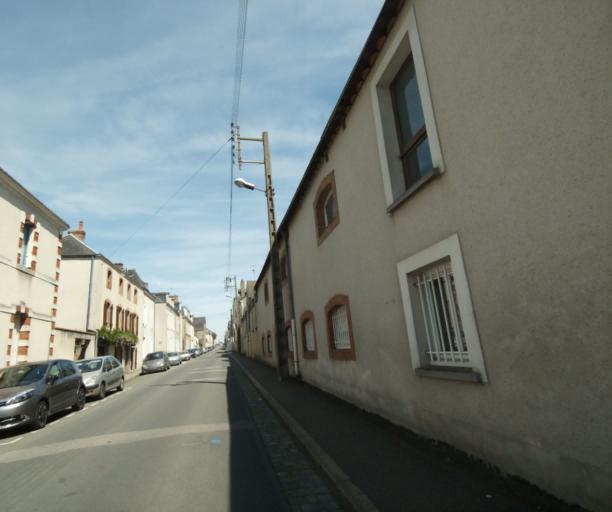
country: FR
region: Pays de la Loire
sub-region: Departement de la Mayenne
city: Laval
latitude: 48.0751
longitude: -0.7691
